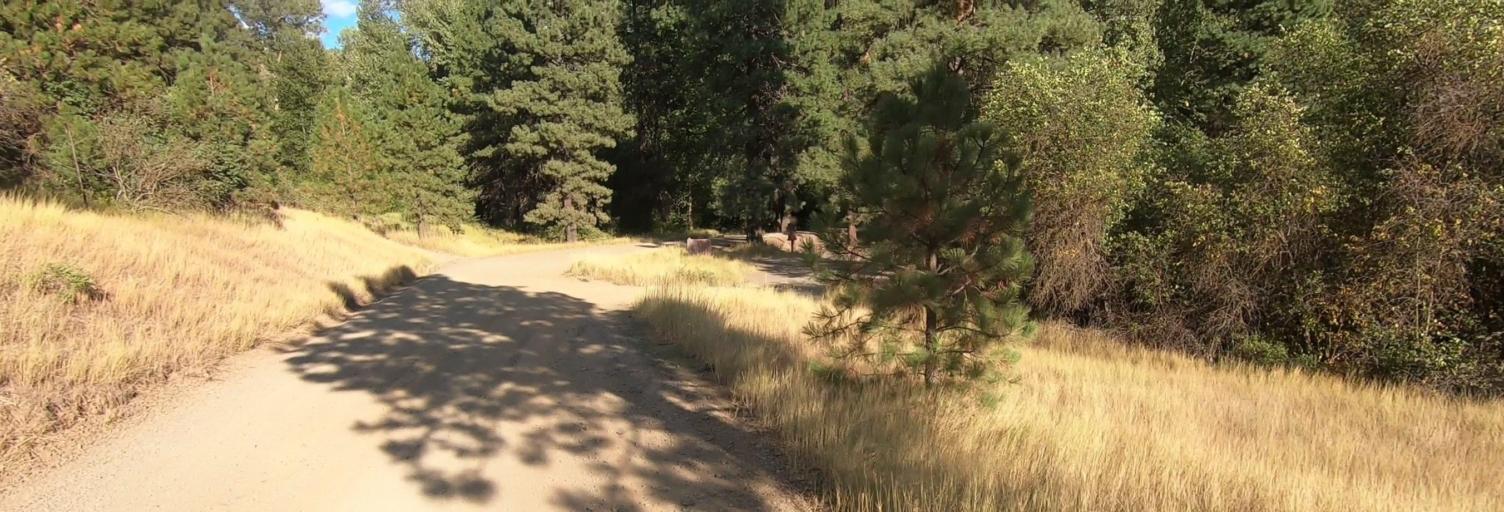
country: US
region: Washington
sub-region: Kittitas County
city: Cle Elum
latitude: 47.2467
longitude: -120.6822
